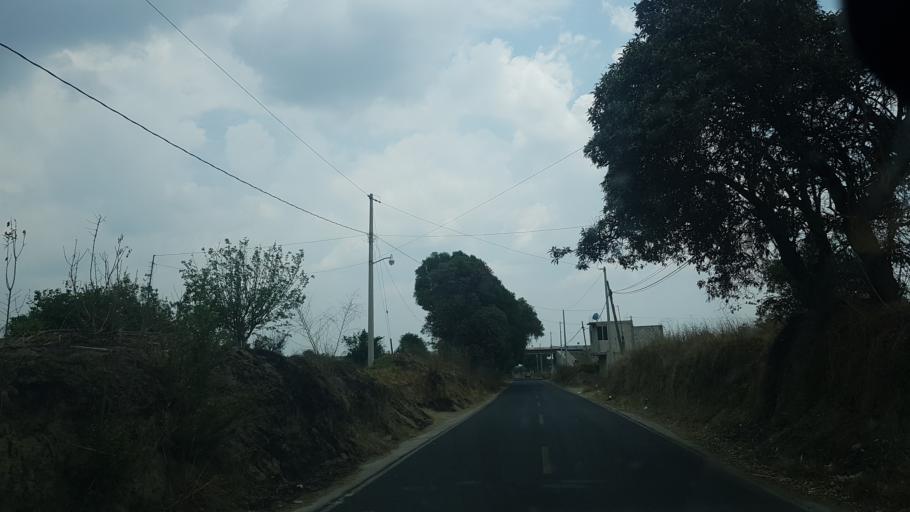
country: MX
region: Puebla
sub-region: Huejotzingo
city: San Miguel Tianguizolco
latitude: 19.1591
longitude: -98.4267
